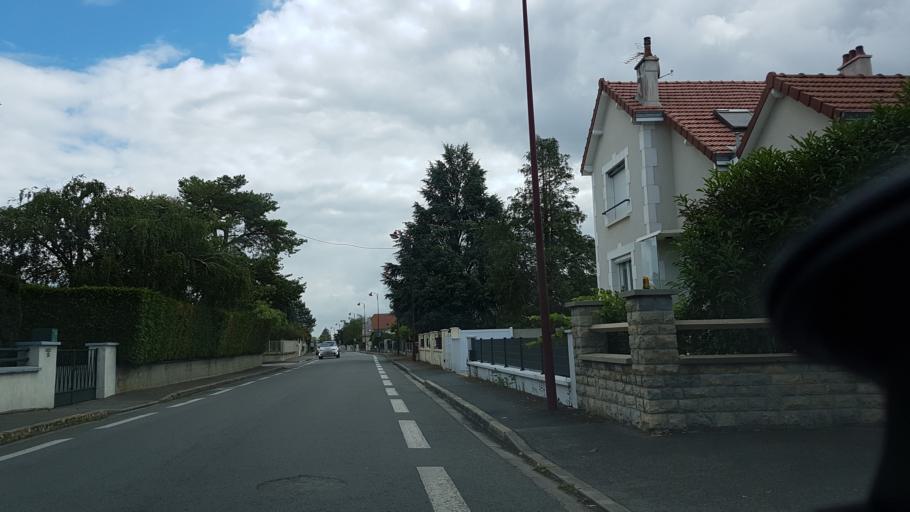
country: FR
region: Centre
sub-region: Departement du Cher
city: Saint-Doulchard
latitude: 47.1055
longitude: 2.3635
